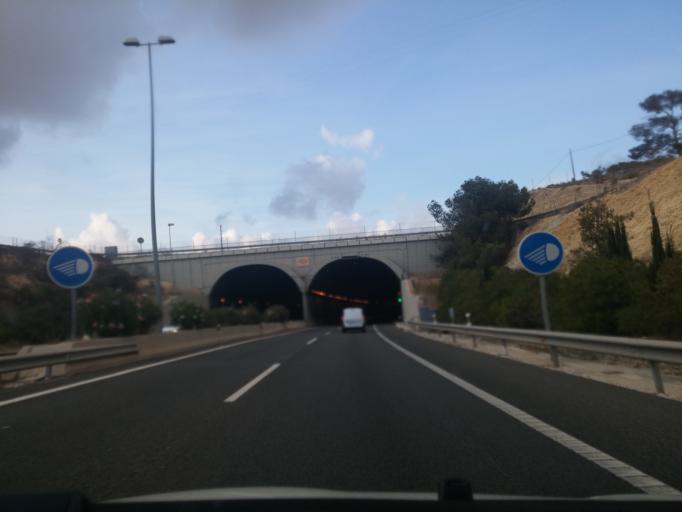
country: ES
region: Valencia
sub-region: Provincia de Alicante
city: San Juan de Alicante
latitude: 38.4023
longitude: -0.4487
